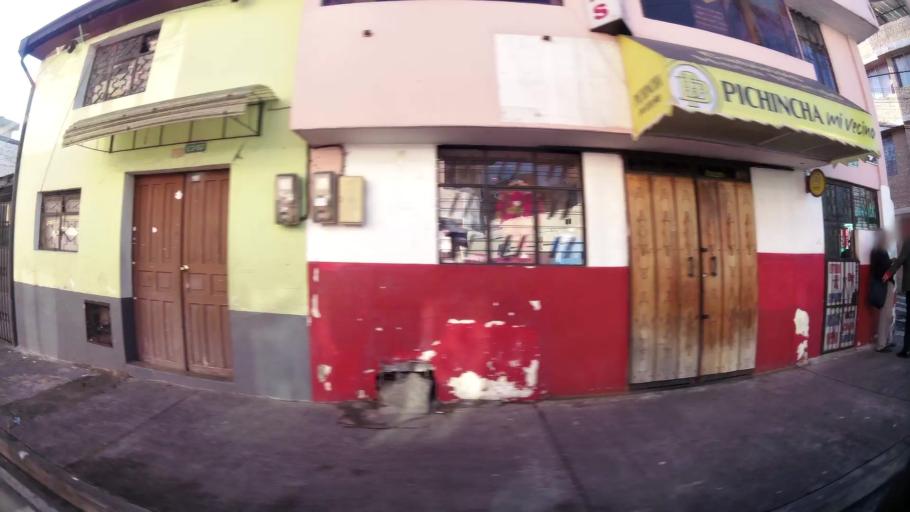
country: EC
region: Pichincha
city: Quito
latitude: -0.2400
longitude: -78.5136
